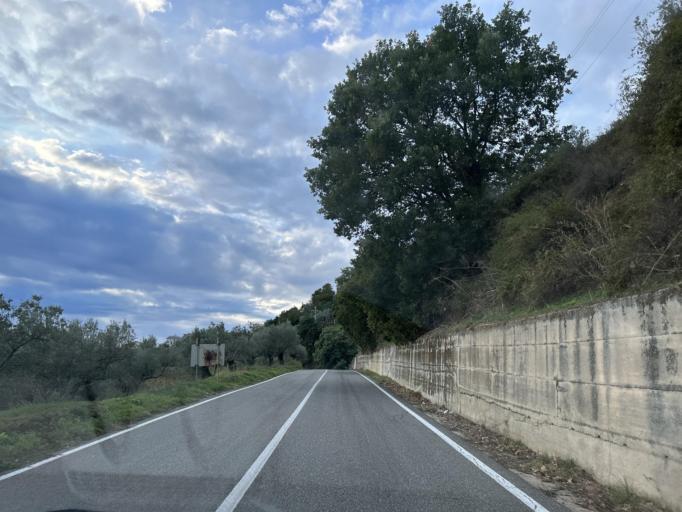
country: IT
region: Calabria
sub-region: Provincia di Catanzaro
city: Montauro
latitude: 38.7526
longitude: 16.5070
